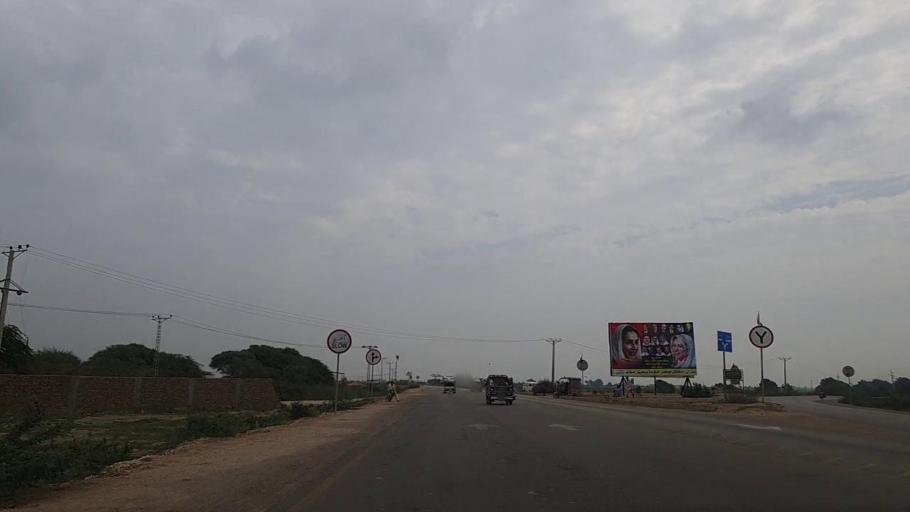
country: PK
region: Sindh
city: Thatta
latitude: 24.6153
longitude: 68.0548
